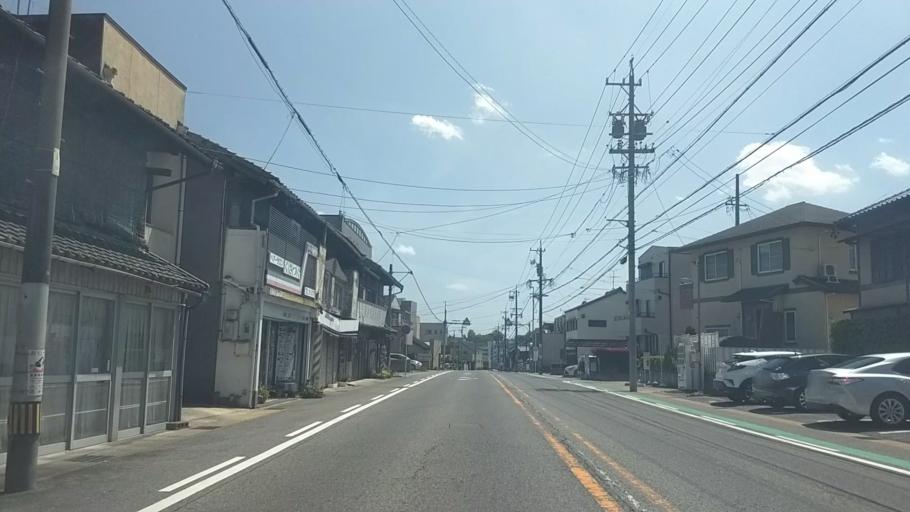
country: JP
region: Aichi
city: Okazaki
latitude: 34.9760
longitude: 137.1691
